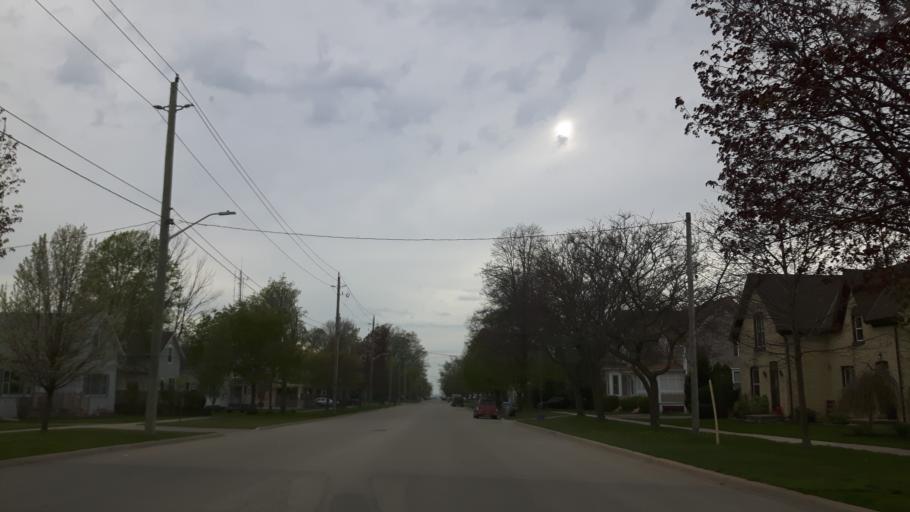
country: CA
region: Ontario
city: Goderich
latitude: 43.7406
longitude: -81.7153
